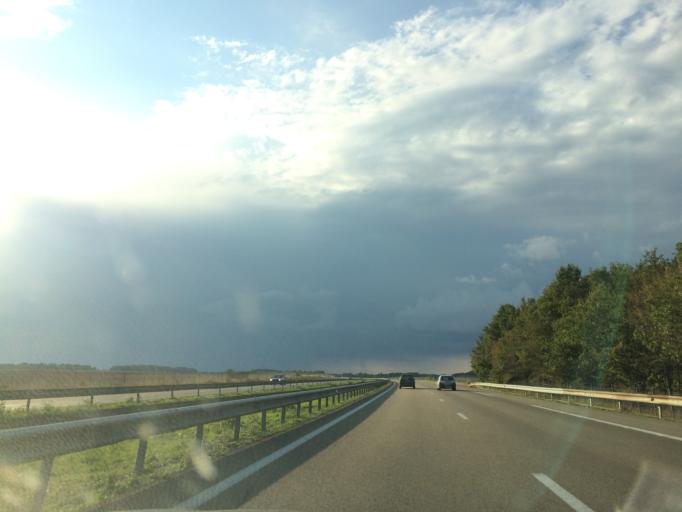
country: FR
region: Bourgogne
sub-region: Departement de l'Yonne
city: Cheroy
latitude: 48.1304
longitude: 2.9552
